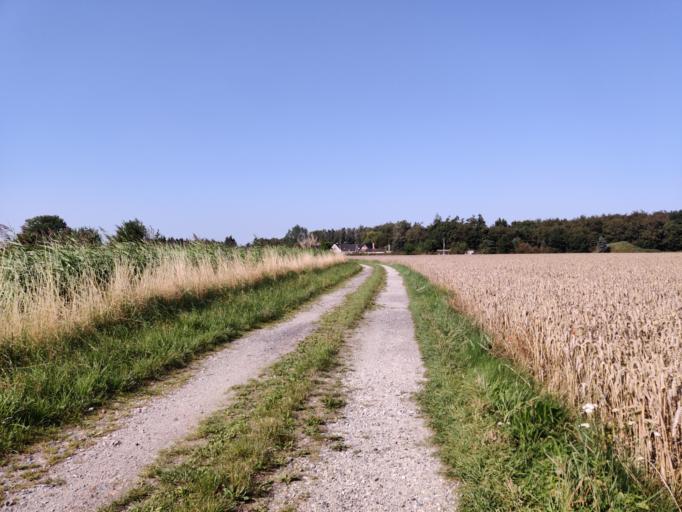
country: DK
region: Zealand
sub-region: Guldborgsund Kommune
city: Nykobing Falster
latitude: 54.6787
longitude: 11.9096
